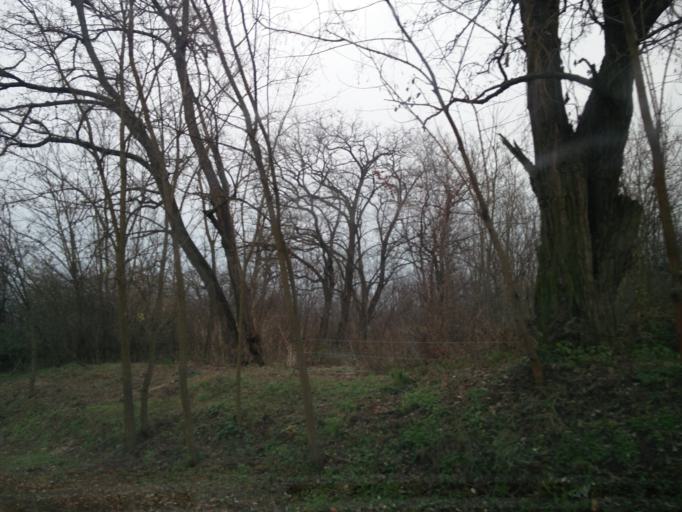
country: HU
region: Pest
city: Fot
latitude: 47.6575
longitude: 19.2237
